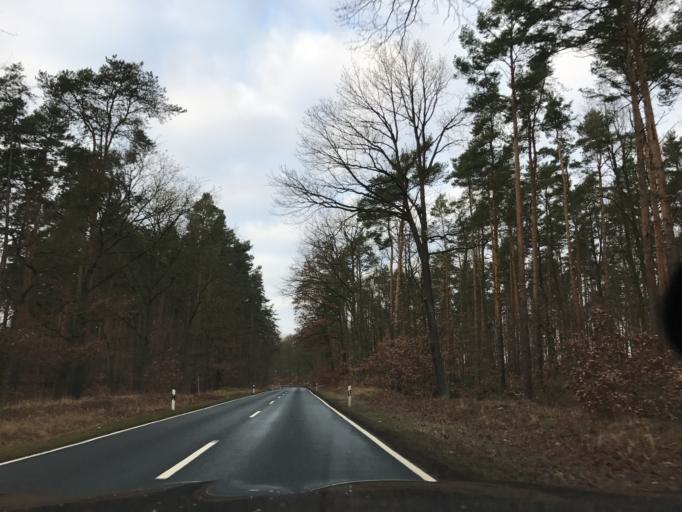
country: DE
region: Brandenburg
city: Gross Kreutz
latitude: 52.3336
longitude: 12.7184
